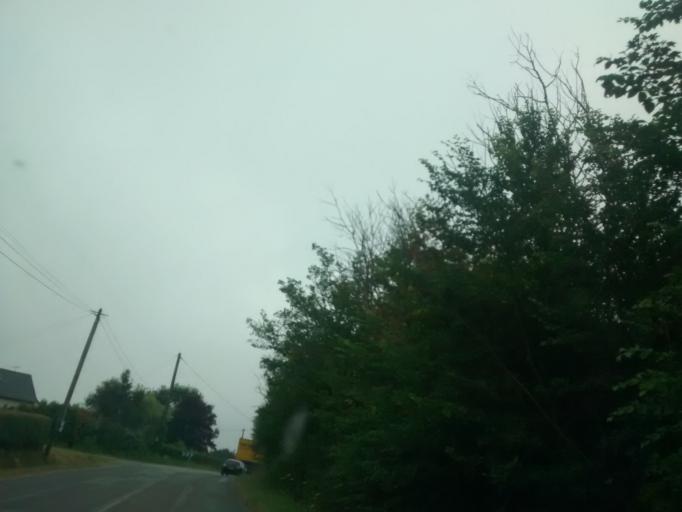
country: FR
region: Brittany
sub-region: Departement d'Ille-et-Vilaine
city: Vezin-le-Coquet
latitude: 48.0882
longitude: -1.7572
